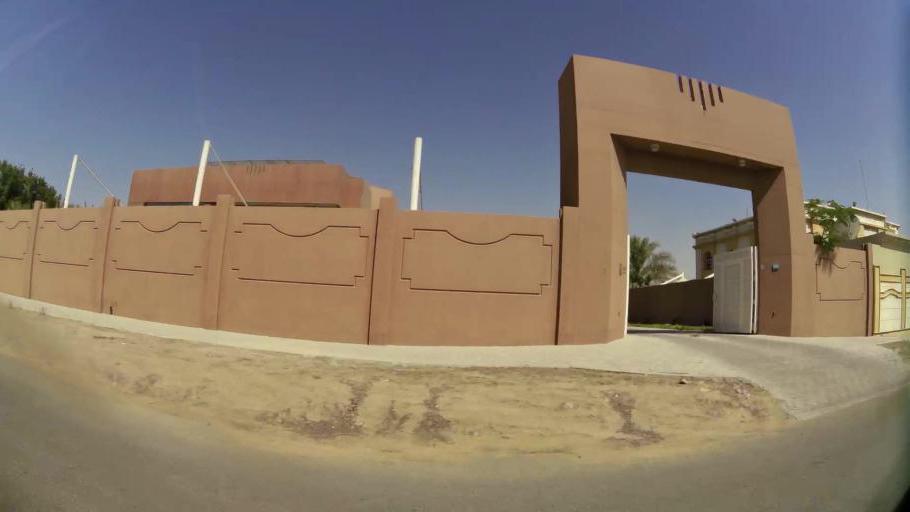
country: AE
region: Ajman
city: Ajman
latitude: 25.4059
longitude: 55.4784
